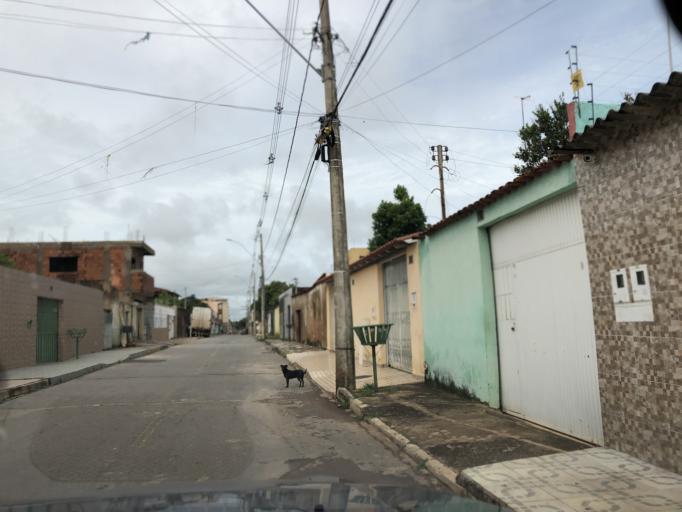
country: BR
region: Federal District
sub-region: Brasilia
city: Brasilia
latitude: -15.7825
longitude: -48.1376
